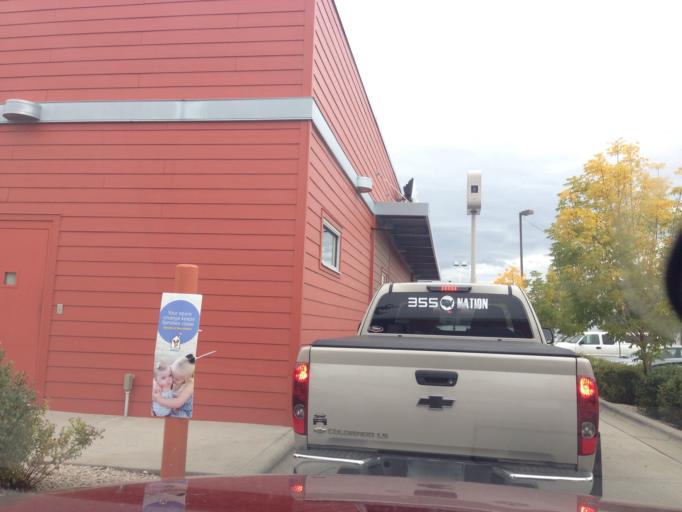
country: US
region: Montana
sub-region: Yellowstone County
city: Laurel
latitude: 45.6659
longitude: -108.7684
